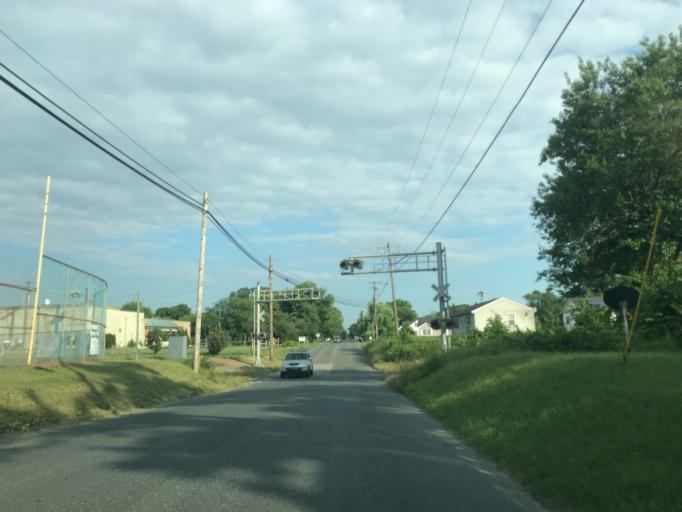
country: US
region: Maryland
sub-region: Caroline County
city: Federalsburg
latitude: 38.6920
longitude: -75.7679
